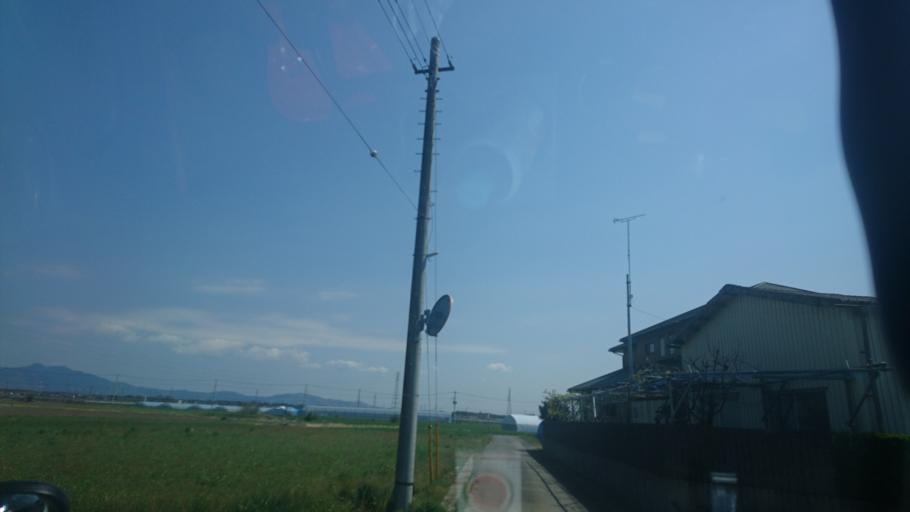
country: JP
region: Ibaraki
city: Ishige
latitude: 36.0820
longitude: 139.9759
